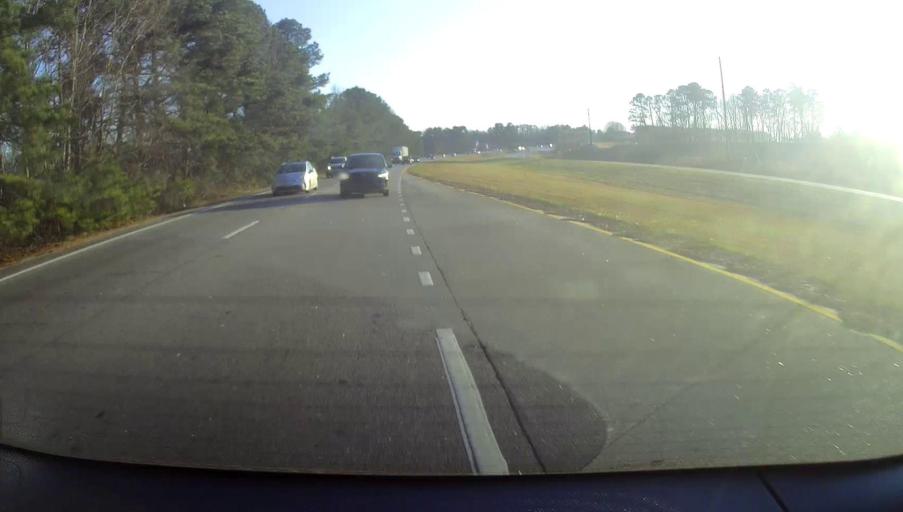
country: US
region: Georgia
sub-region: Fayette County
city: Tyrone
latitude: 33.4998
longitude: -84.5766
